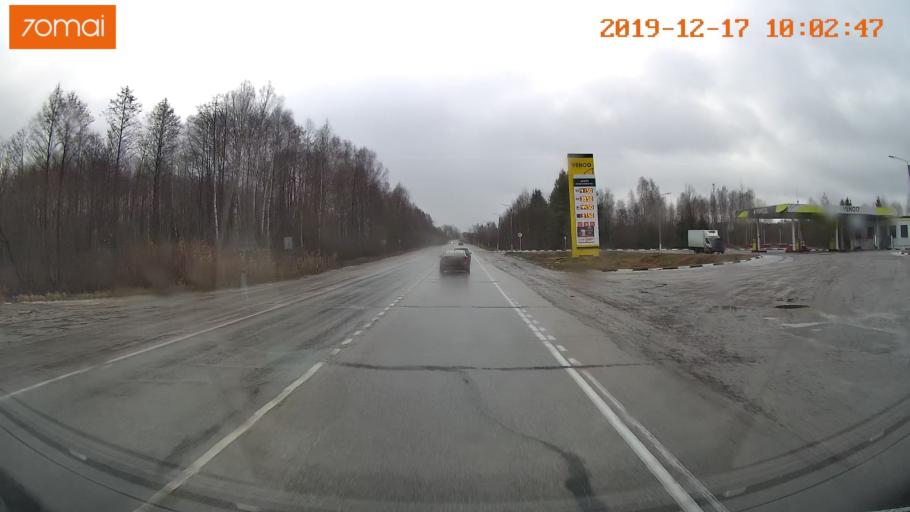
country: RU
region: Vladimir
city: Golovino
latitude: 55.9225
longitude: 40.6020
